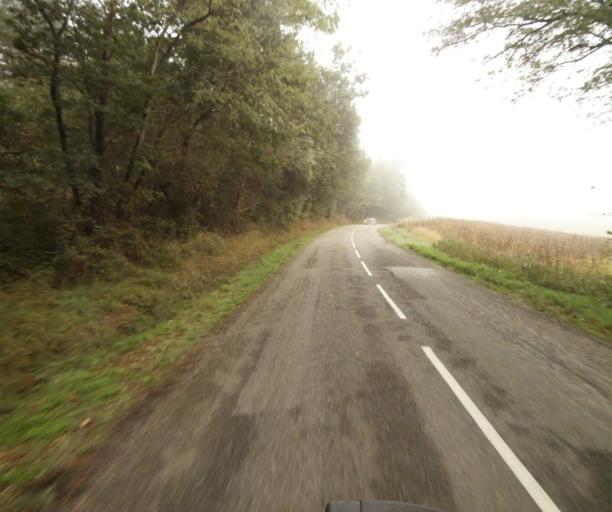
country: FR
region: Midi-Pyrenees
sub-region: Departement du Tarn-et-Garonne
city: Saint-Nauphary
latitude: 43.9386
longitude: 1.4611
